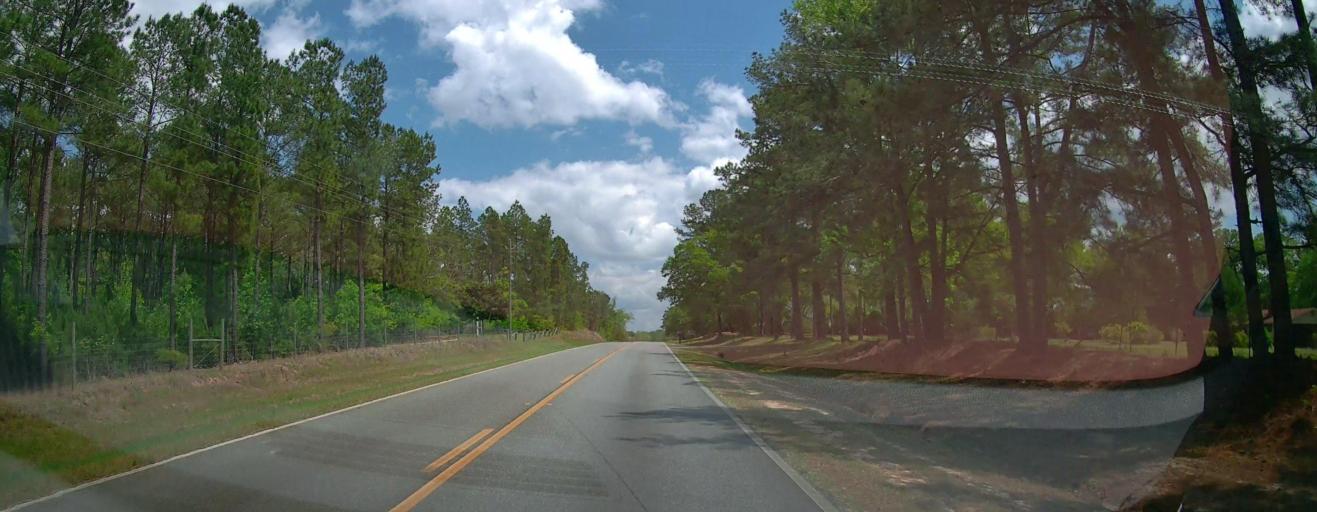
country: US
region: Georgia
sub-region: Laurens County
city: East Dublin
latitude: 32.5253
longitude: -82.7435
